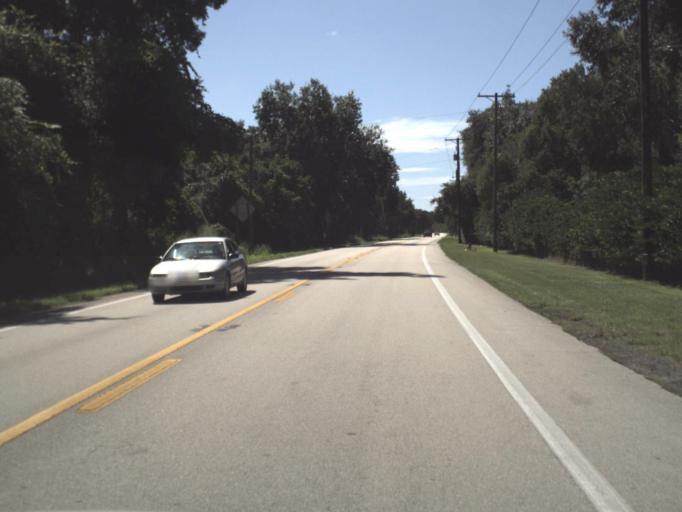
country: US
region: Florida
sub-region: Polk County
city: Polk City
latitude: 28.1405
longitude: -81.7967
